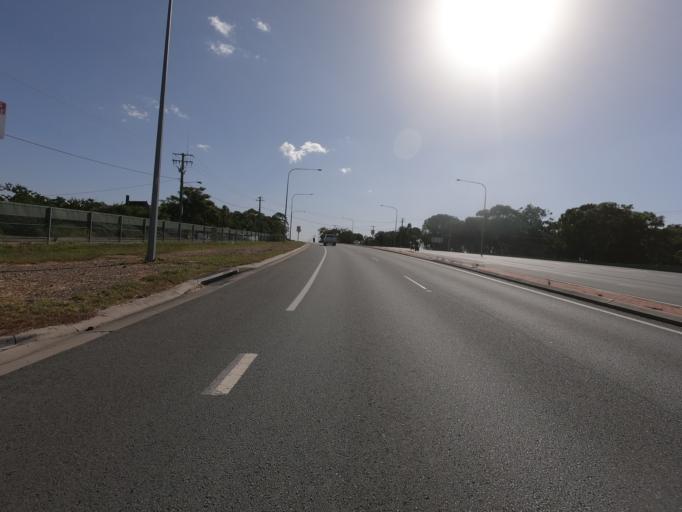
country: AU
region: Queensland
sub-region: Brisbane
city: Mackenzie
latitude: -27.5473
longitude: 153.1337
